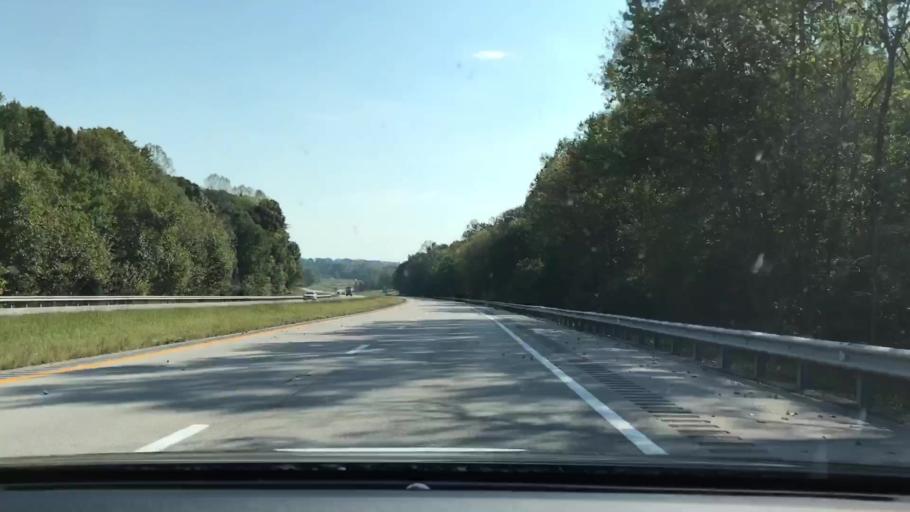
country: US
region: Kentucky
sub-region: Pulaski County
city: Somerset
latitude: 37.0917
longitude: -84.8124
